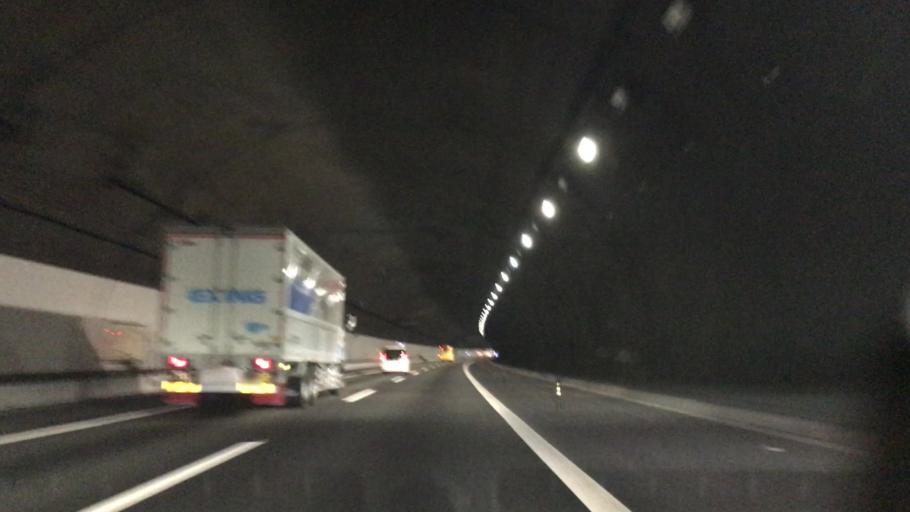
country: JP
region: Shiga Prefecture
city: Kusatsu
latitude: 34.9498
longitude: 136.0202
